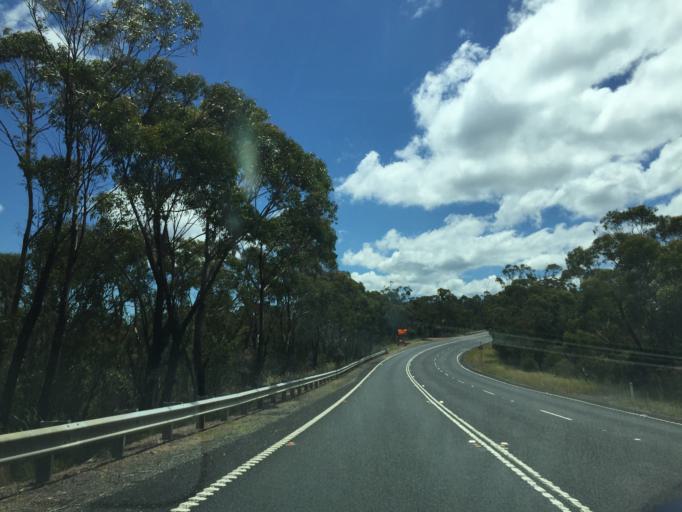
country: AU
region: New South Wales
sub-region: Blue Mountains Municipality
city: Blackheath
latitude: -33.5669
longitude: 150.3468
